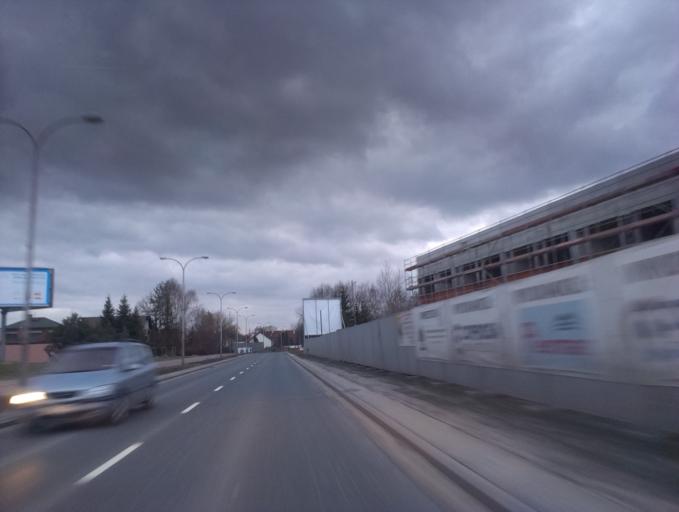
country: PL
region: Masovian Voivodeship
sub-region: Powiat piaseczynski
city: Konstancin-Jeziorna
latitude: 52.0926
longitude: 21.1154
